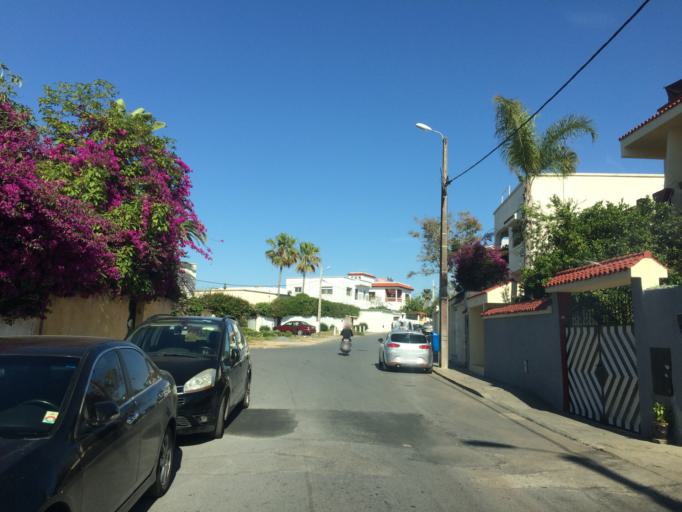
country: MA
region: Rabat-Sale-Zemmour-Zaer
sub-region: Rabat
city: Rabat
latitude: 33.9887
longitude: -6.8233
